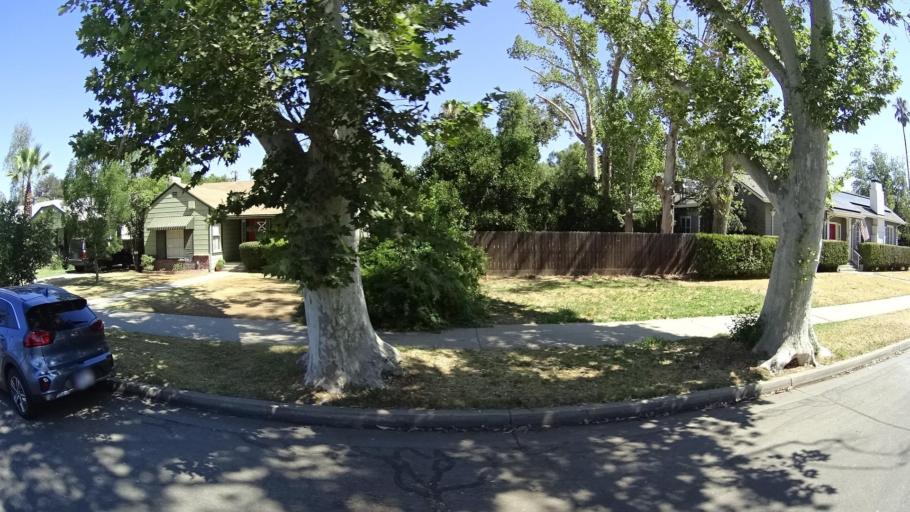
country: US
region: California
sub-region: Fresno County
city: Fresno
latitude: 36.7381
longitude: -119.7616
